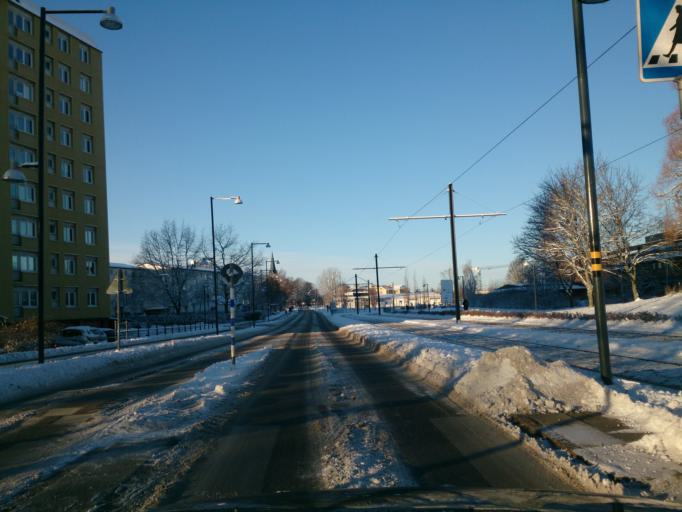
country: SE
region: OEstergoetland
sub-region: Norrkopings Kommun
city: Norrkoping
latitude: 58.5737
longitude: 16.2043
